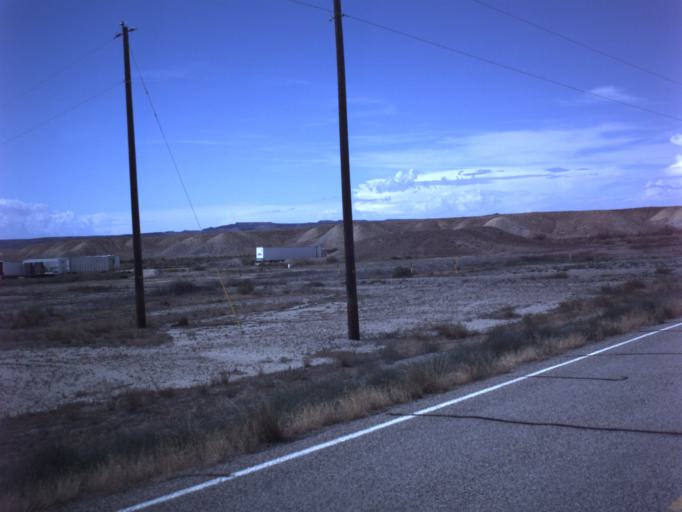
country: US
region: Utah
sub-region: Grand County
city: Moab
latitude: 38.9383
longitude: -109.3924
